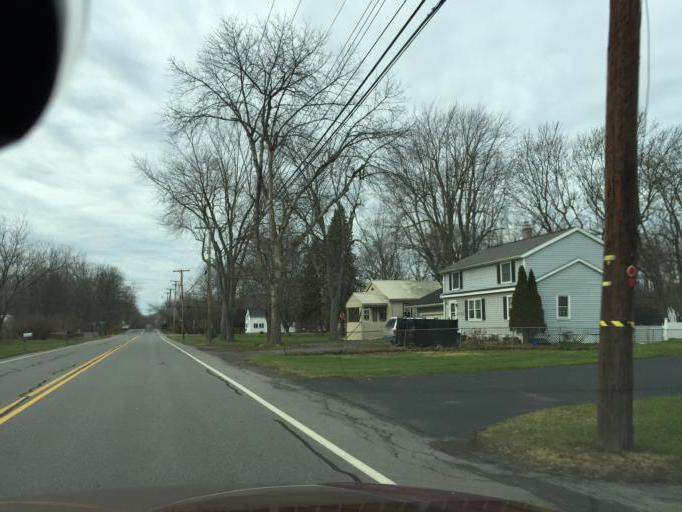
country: US
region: New York
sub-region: Monroe County
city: North Gates
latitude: 43.0934
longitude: -77.6887
